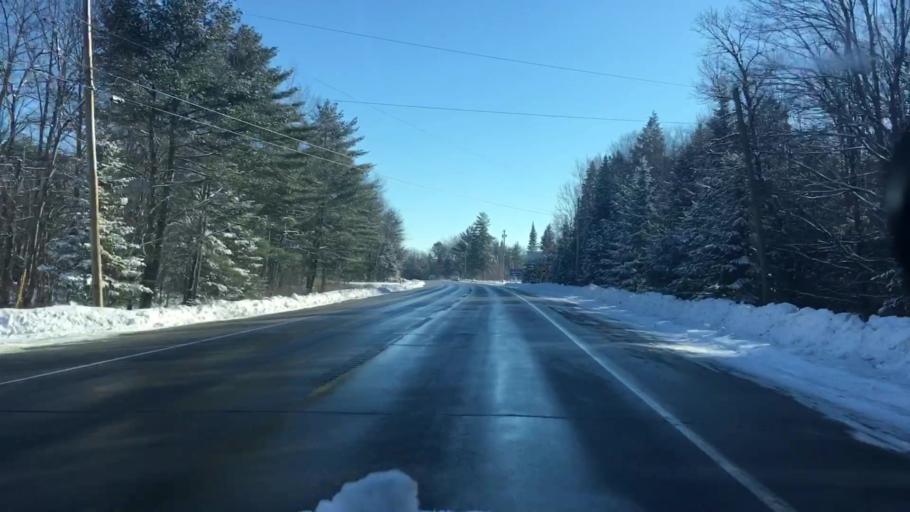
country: US
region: Maine
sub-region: Cumberland County
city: Bridgton
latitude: 44.0109
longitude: -70.6782
